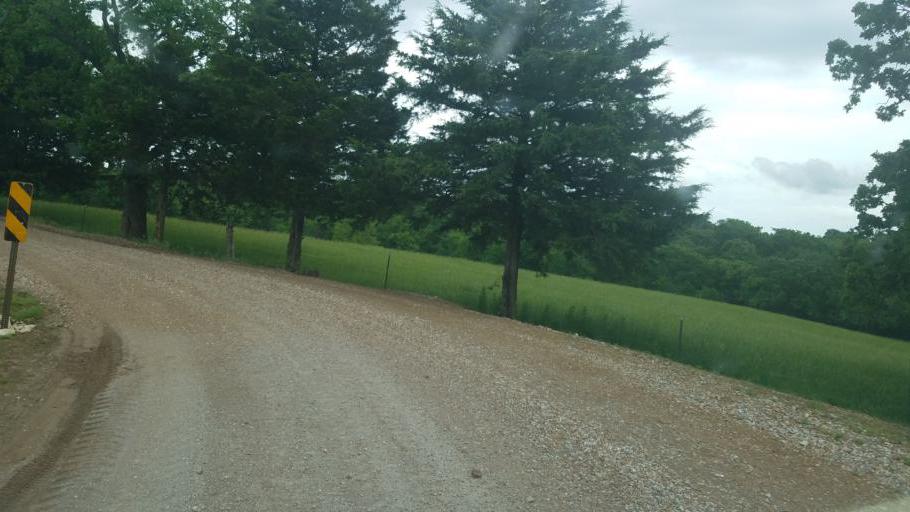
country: US
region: Missouri
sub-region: Moniteau County
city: California
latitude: 38.5905
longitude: -92.6589
